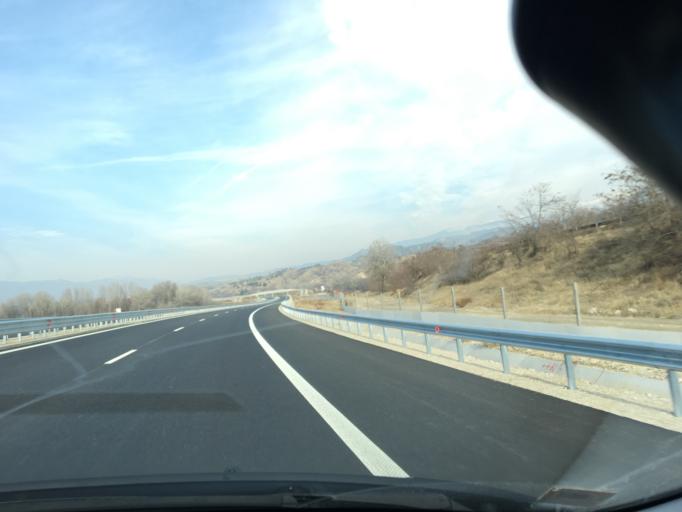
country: BG
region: Blagoevgrad
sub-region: Obshtina Strumyani
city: Strumyani
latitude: 41.5997
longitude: 23.2251
